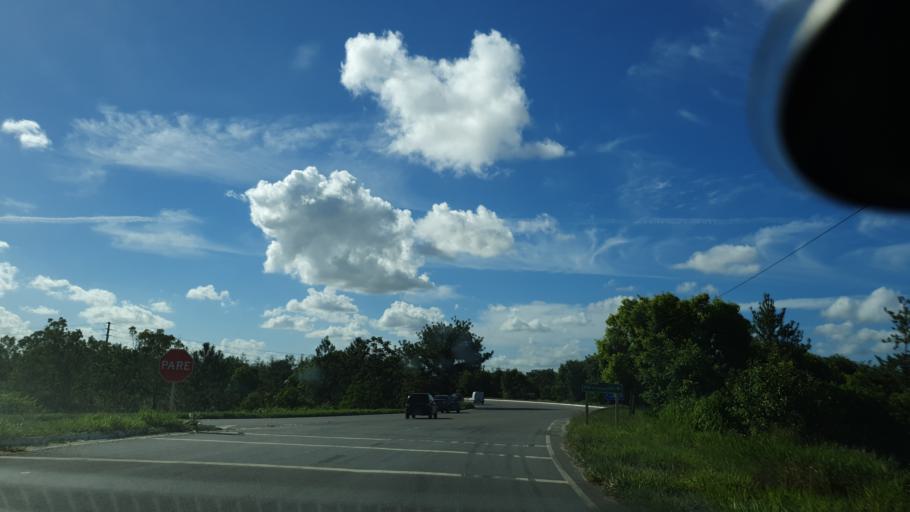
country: BR
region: Bahia
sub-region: Camacari
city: Camacari
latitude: -12.6823
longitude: -38.3016
